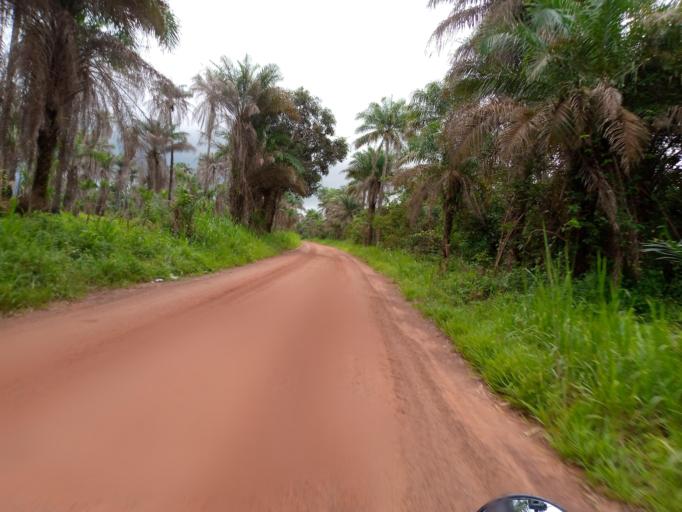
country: SL
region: Northern Province
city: Port Loko
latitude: 8.8748
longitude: -12.7266
